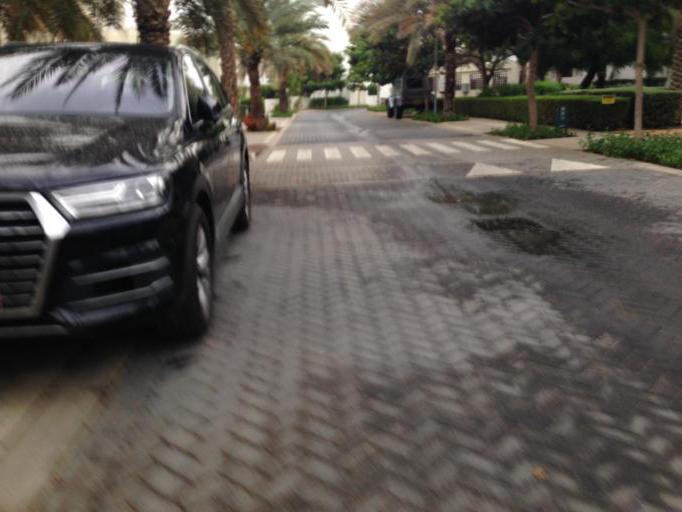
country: OM
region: Muhafazat Masqat
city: As Sib al Jadidah
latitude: 23.6263
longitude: 58.2698
